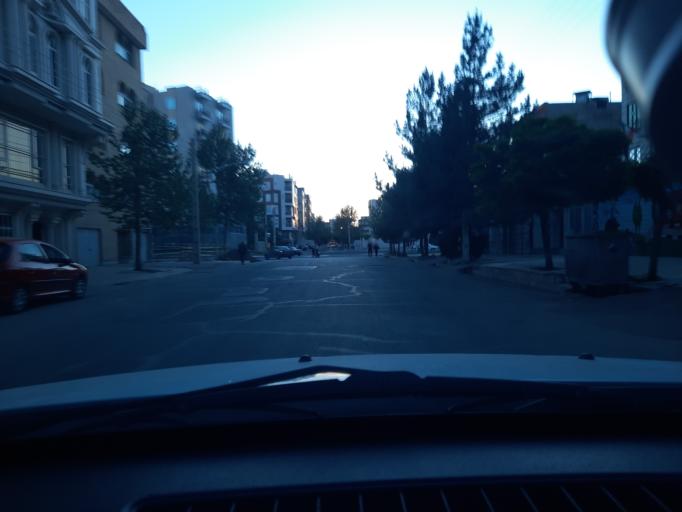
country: IR
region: Qazvin
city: Qazvin
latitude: 36.2991
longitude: 50.0129
